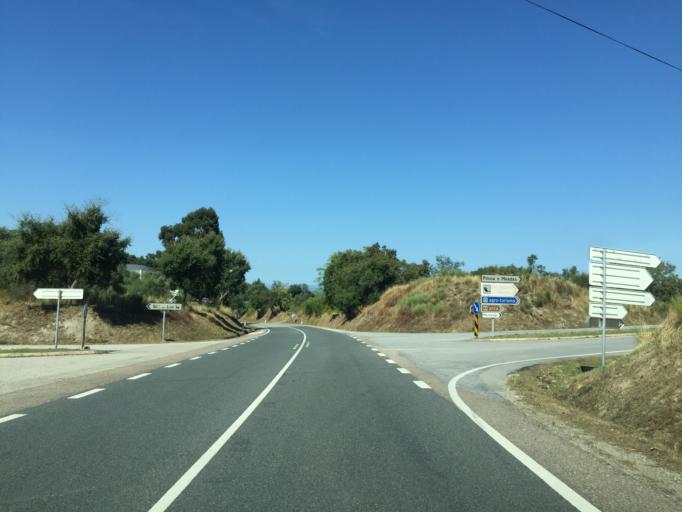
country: PT
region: Portalegre
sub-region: Castelo de Vide
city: Castelo de Vide
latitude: 39.4238
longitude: -7.4760
